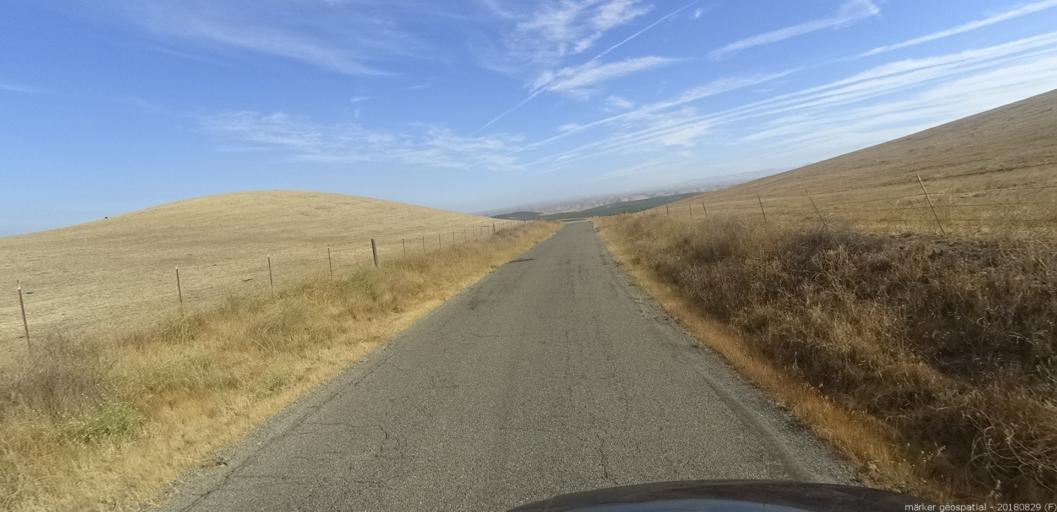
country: US
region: California
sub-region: Monterey County
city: King City
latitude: 36.0473
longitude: -120.9777
